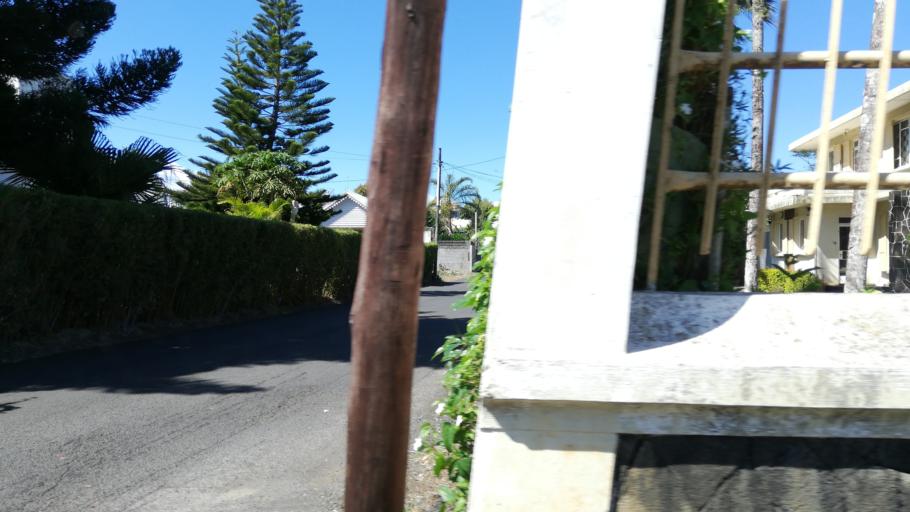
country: MU
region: Plaines Wilhems
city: Ebene
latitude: -20.2335
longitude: 57.4765
